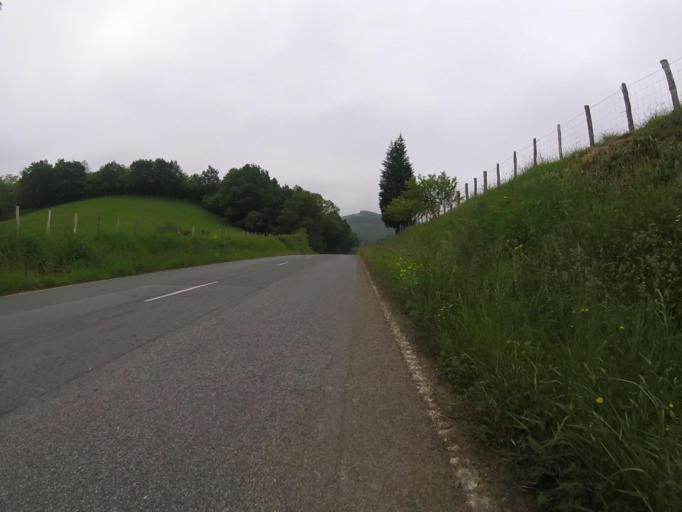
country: ES
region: Navarre
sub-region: Provincia de Navarra
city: Zugarramurdi
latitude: 43.2740
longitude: -1.4962
